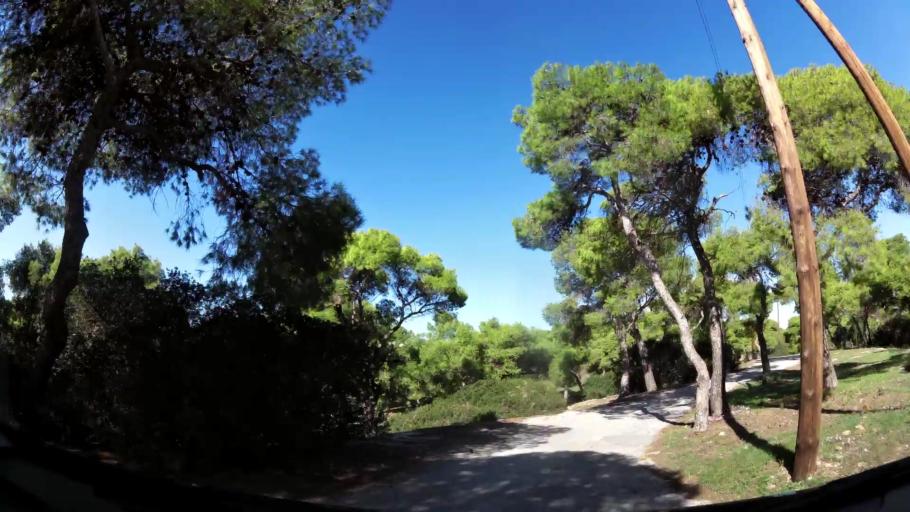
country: GR
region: Attica
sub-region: Nomarchia Anatolikis Attikis
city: Vouliagmeni
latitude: 37.8146
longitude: 23.7754
